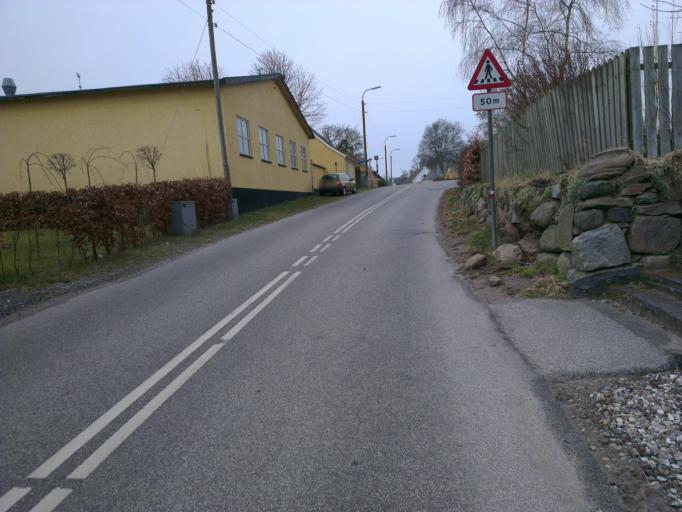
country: DK
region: Capital Region
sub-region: Frederikssund Kommune
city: Skibby
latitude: 55.7943
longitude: 11.9565
